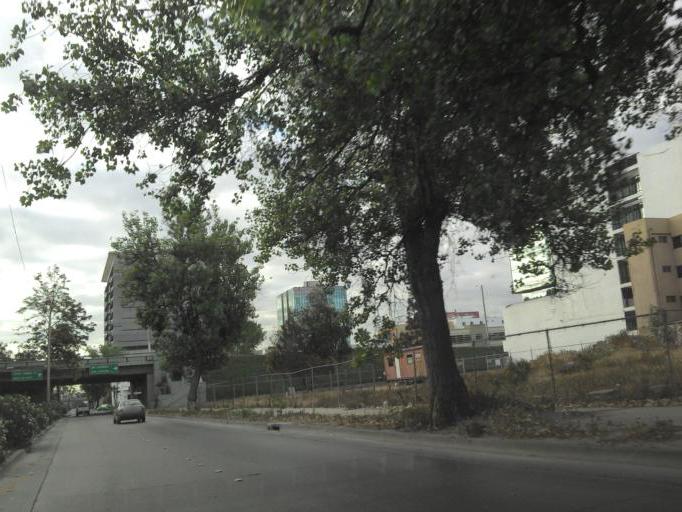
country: MX
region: Baja California
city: Tijuana
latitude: 32.5229
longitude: -117.0096
